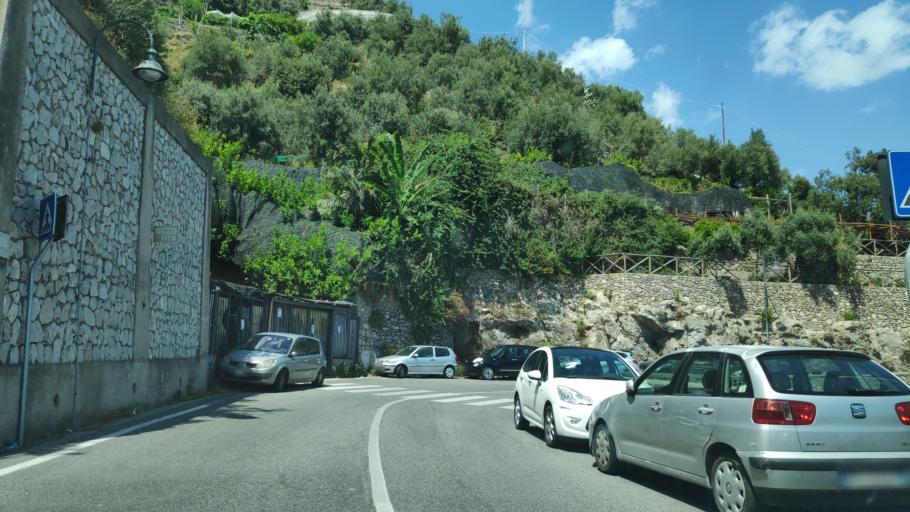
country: IT
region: Campania
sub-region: Provincia di Salerno
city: Ravello
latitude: 40.6438
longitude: 14.6180
